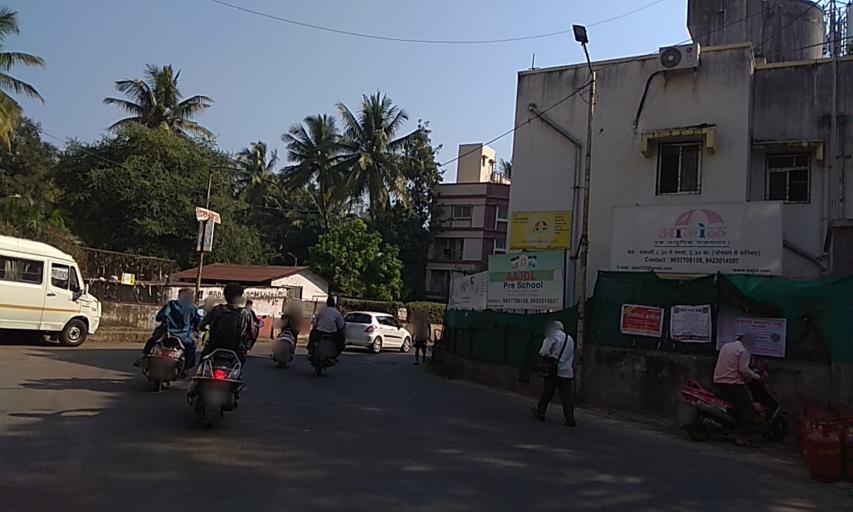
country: IN
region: Maharashtra
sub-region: Pune Division
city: Pune
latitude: 18.4783
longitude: 73.8216
